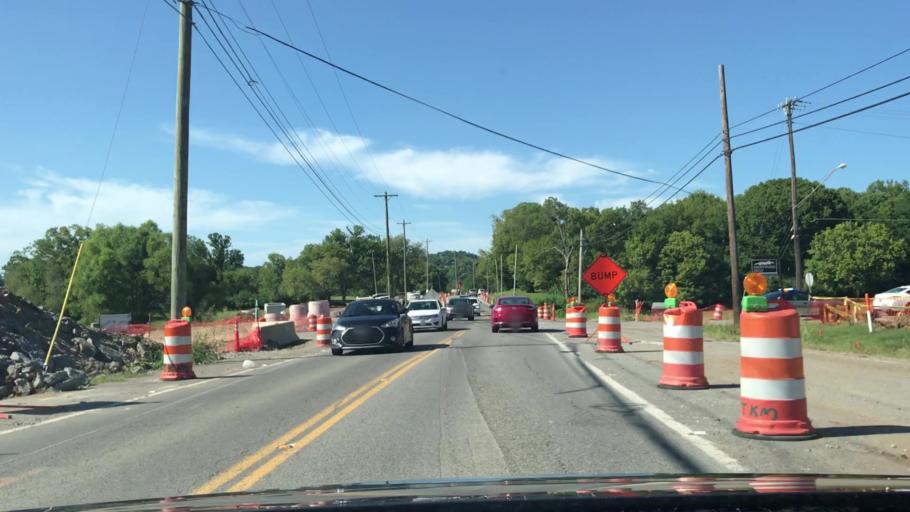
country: US
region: Tennessee
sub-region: Williamson County
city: Brentwood Estates
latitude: 35.9933
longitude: -86.8124
